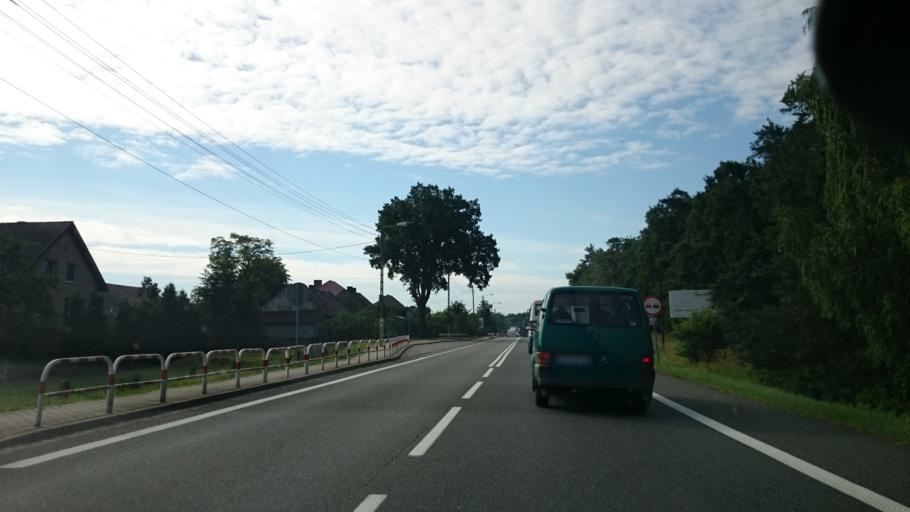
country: PL
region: Opole Voivodeship
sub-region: Powiat opolski
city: Tarnow Opolski
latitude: 50.6086
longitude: 18.0715
